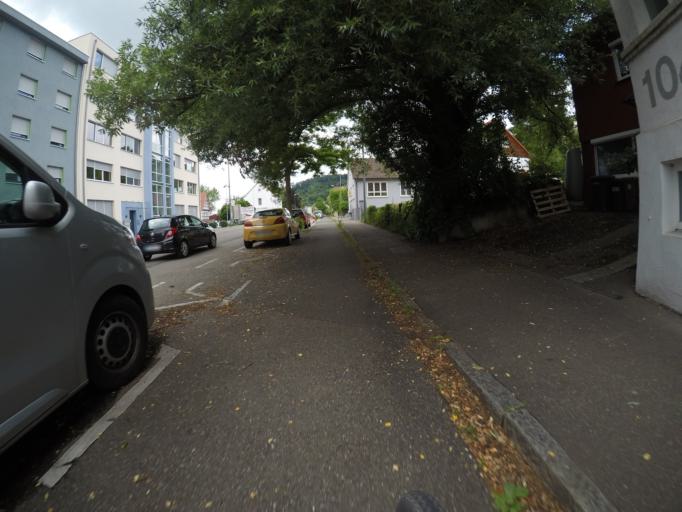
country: DE
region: Baden-Wuerttemberg
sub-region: Regierungsbezirk Stuttgart
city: Plochingen
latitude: 48.7171
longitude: 9.4132
